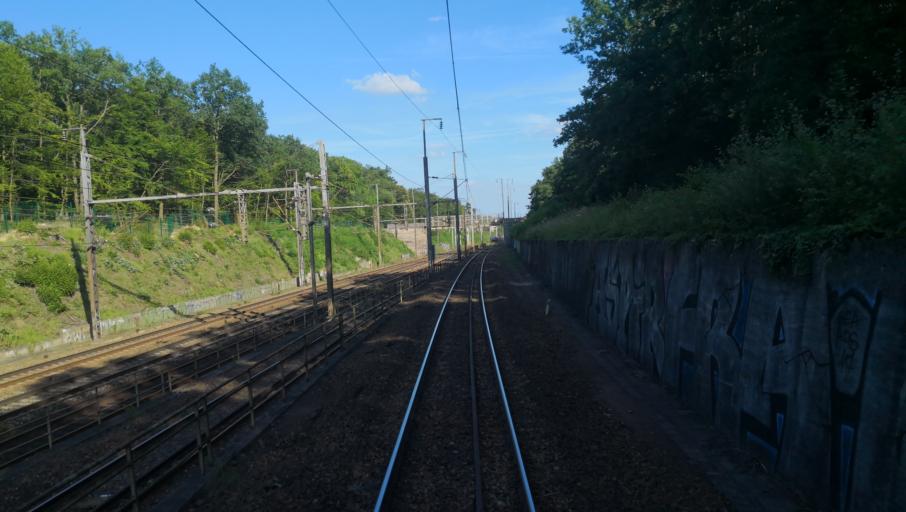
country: FR
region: Ile-de-France
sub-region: Departement des Yvelines
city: Maisons-Laffitte
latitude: 48.9553
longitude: 2.1296
